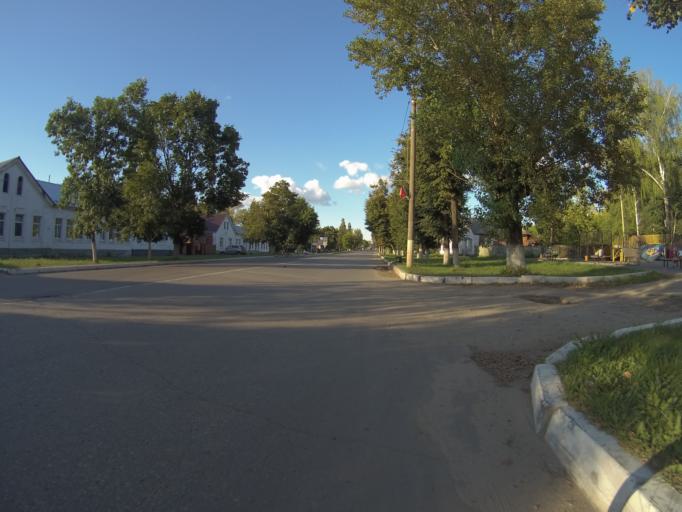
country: RU
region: Vladimir
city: Gus'-Khrustal'nyy
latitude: 55.6169
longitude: 40.6735
